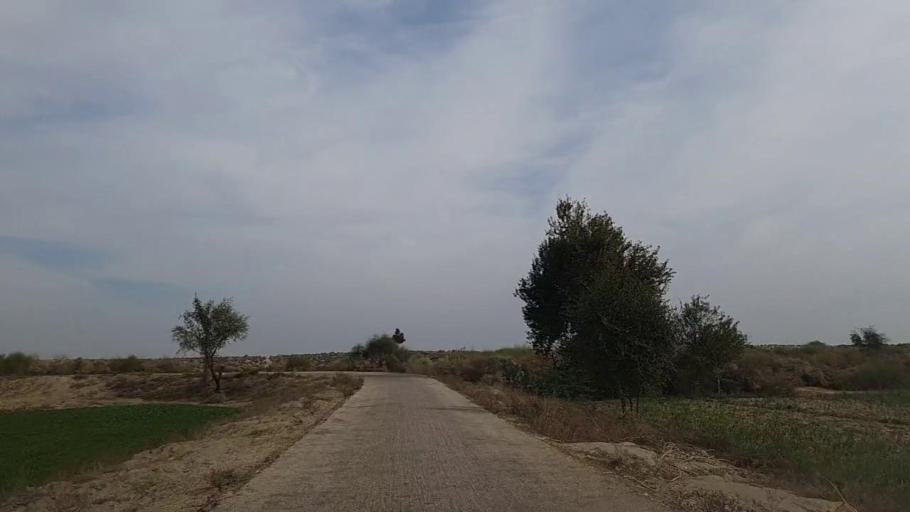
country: PK
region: Sindh
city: Jam Sahib
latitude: 26.4417
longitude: 68.6102
